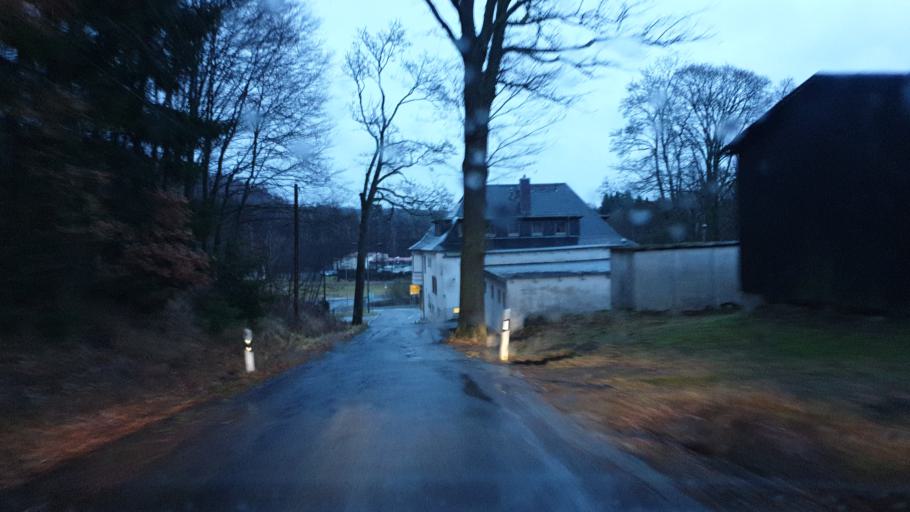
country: DE
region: Saxony
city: Adorf
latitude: 50.3009
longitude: 12.2505
